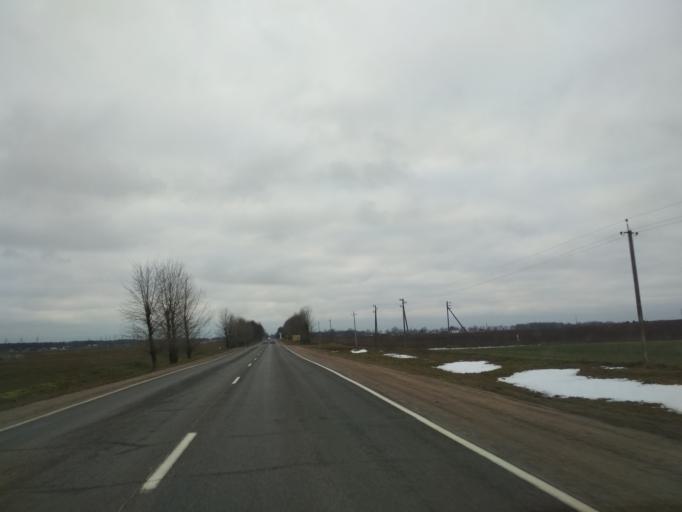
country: BY
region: Minsk
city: Blon'
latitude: 53.5363
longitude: 28.1584
